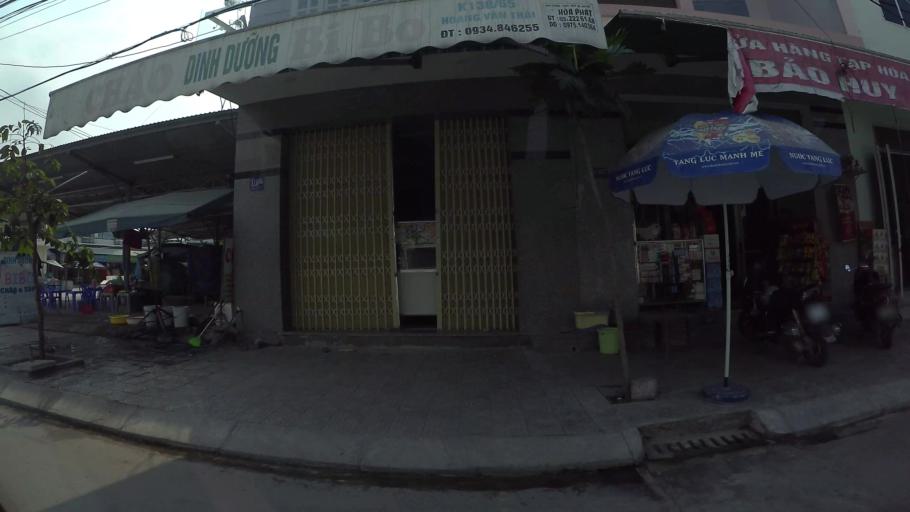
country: VN
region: Da Nang
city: Lien Chieu
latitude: 16.0561
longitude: 108.1567
